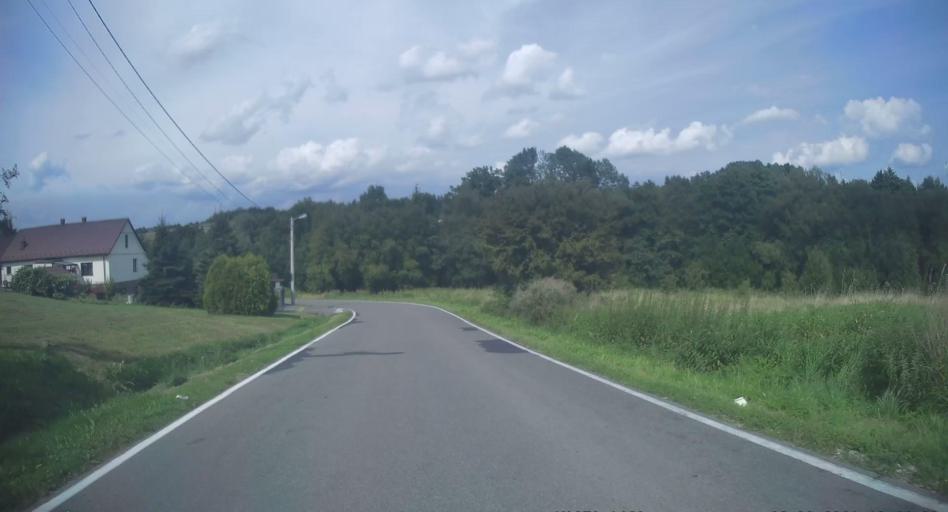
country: PL
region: Lesser Poland Voivodeship
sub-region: Powiat wielicki
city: Pawlikowice
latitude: 49.9500
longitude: 20.0424
